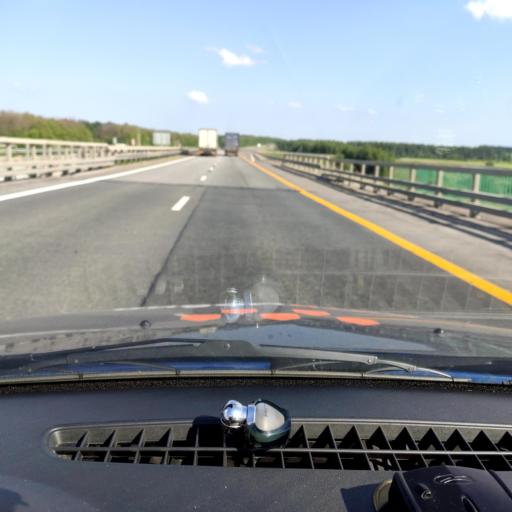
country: RU
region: Lipetsk
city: Yelets
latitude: 52.5387
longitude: 38.7293
